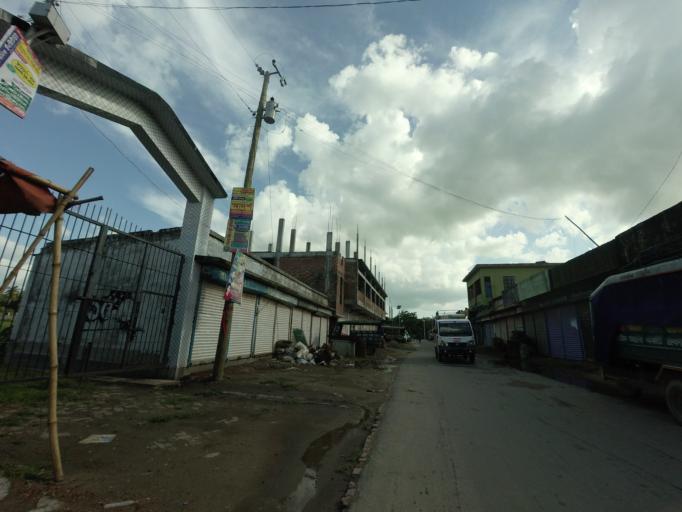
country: BD
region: Khulna
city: Kalia
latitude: 23.0412
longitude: 89.6295
